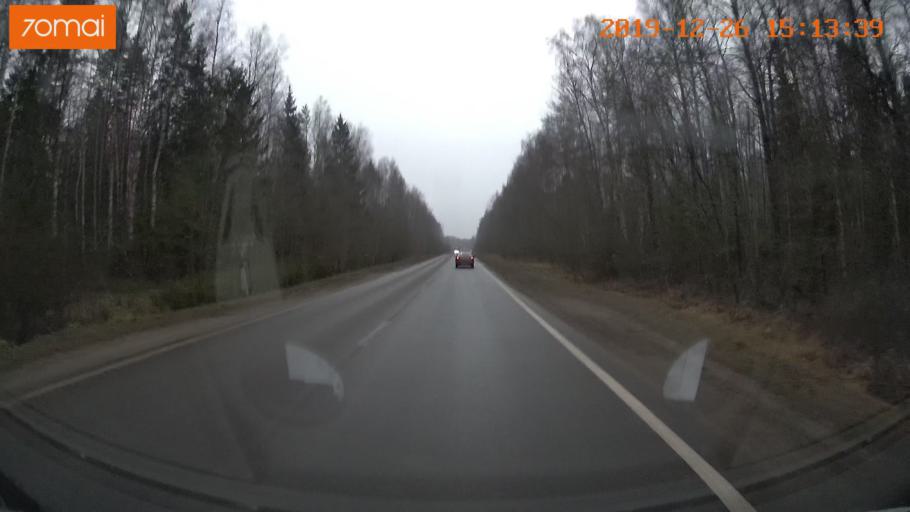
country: RU
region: Jaroslavl
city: Rybinsk
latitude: 58.1143
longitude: 38.8832
